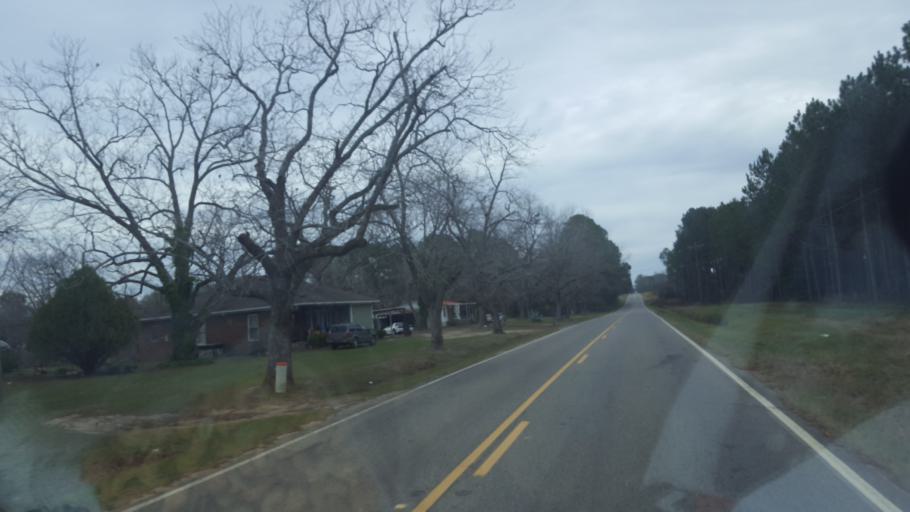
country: US
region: Georgia
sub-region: Ben Hill County
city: Fitzgerald
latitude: 31.7435
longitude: -83.2840
